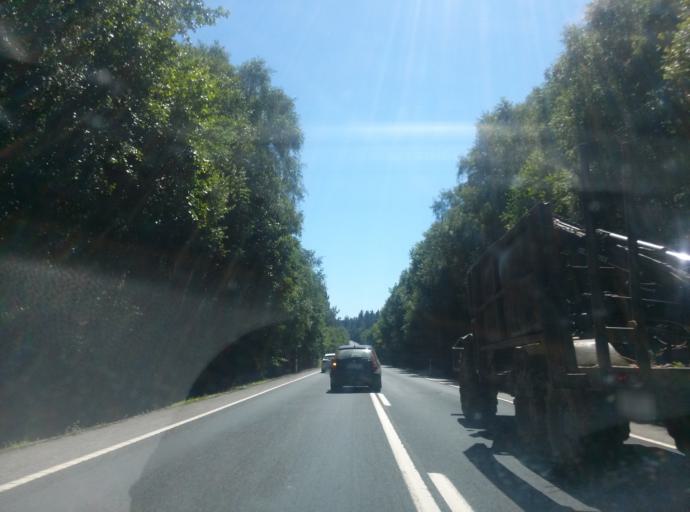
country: ES
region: Galicia
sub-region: Provincia de Lugo
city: Castro de Rei
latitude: 43.1484
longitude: -7.3957
